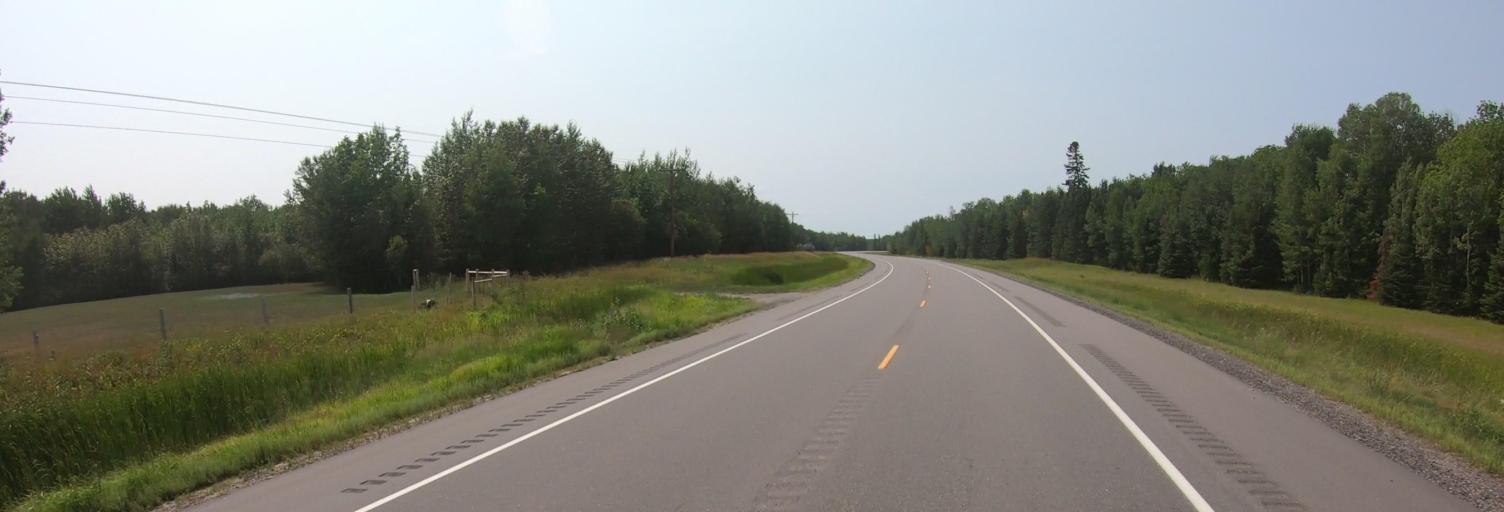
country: US
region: Minnesota
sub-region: Koochiching County
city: International Falls
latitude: 48.5287
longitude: -93.5274
